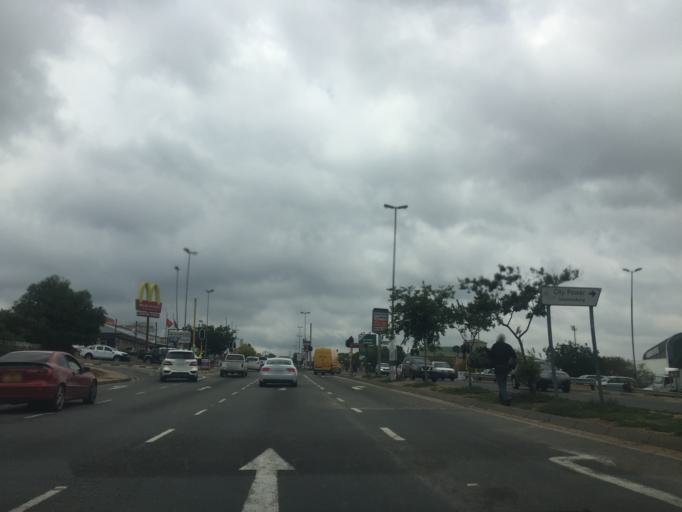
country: ZA
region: Gauteng
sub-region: City of Johannesburg Metropolitan Municipality
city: Johannesburg
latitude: -26.0926
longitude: 27.9836
